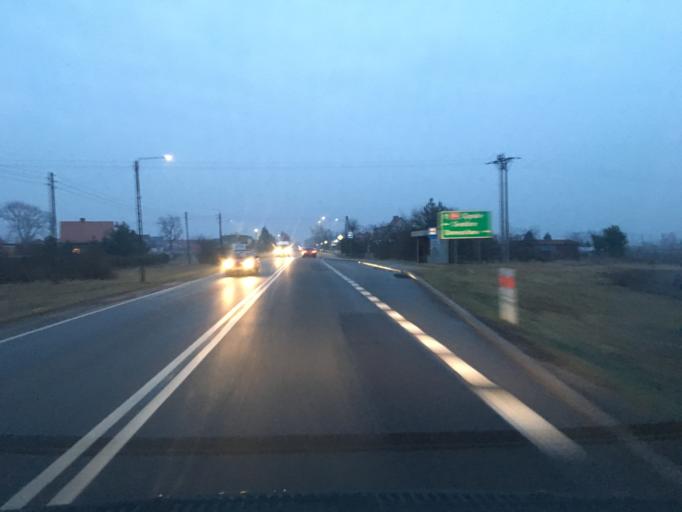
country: PL
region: Lower Silesian Voivodeship
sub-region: Powiat olawski
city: Wierzbno
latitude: 50.9846
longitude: 17.2217
